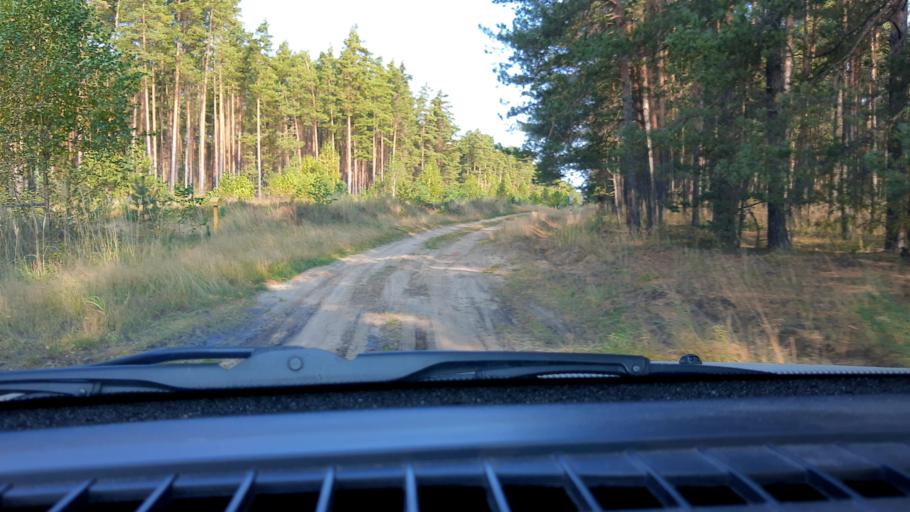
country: RU
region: Nizjnij Novgorod
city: Lukino
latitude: 56.3998
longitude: 43.6417
